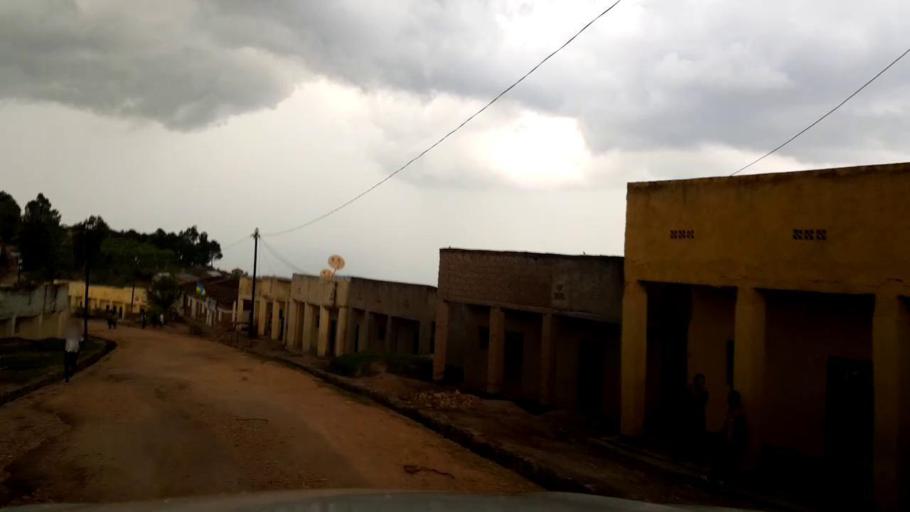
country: RW
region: Southern Province
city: Gitarama
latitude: -1.8709
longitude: 29.5905
